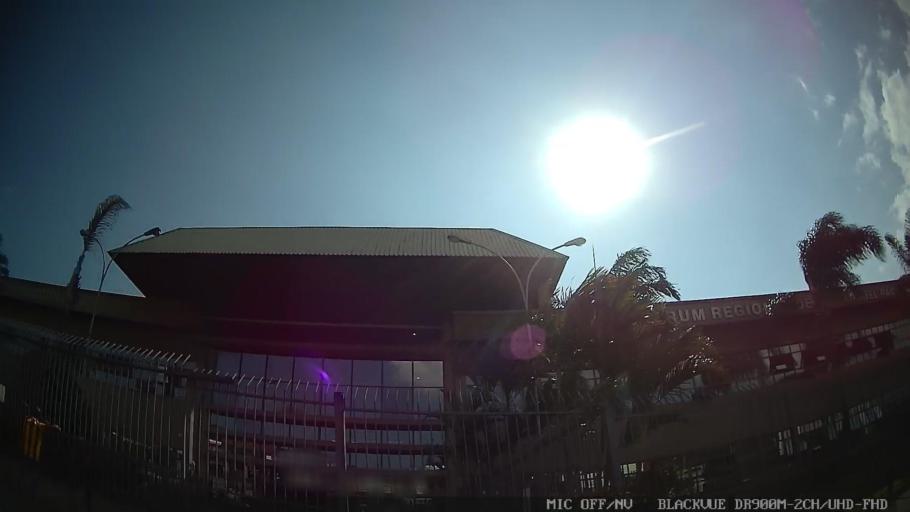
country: BR
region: Sao Paulo
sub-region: Ferraz De Vasconcelos
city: Ferraz de Vasconcelos
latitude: -23.5094
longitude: -46.4446
